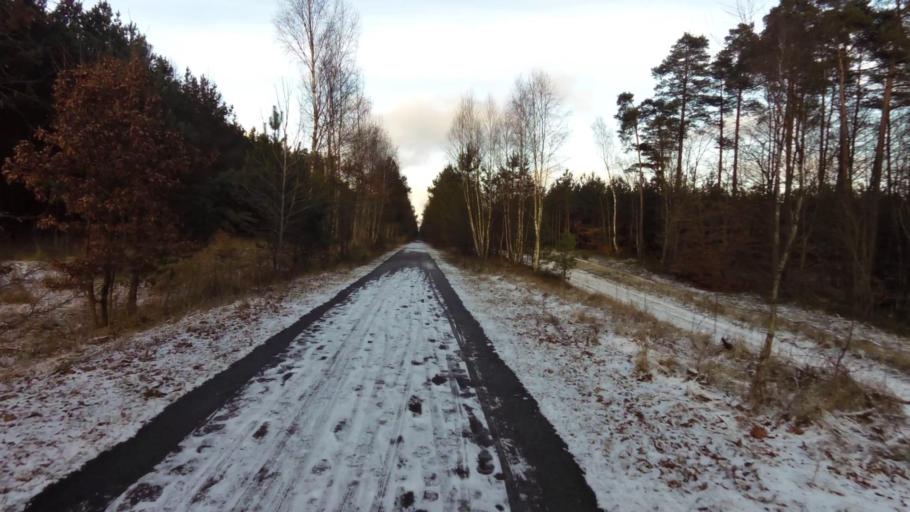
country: PL
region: West Pomeranian Voivodeship
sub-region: Powiat drawski
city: Zlocieniec
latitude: 53.5554
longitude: 16.0253
